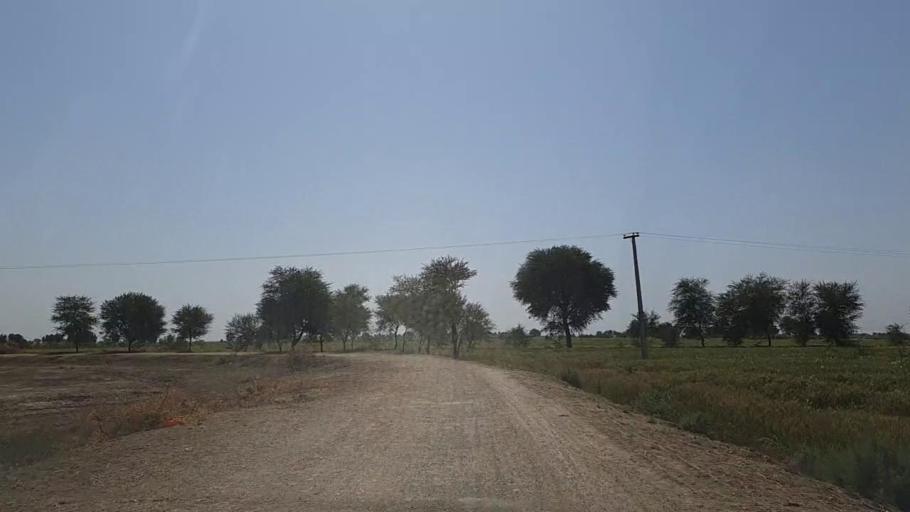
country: PK
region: Sindh
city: Samaro
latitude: 25.2156
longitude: 69.4054
